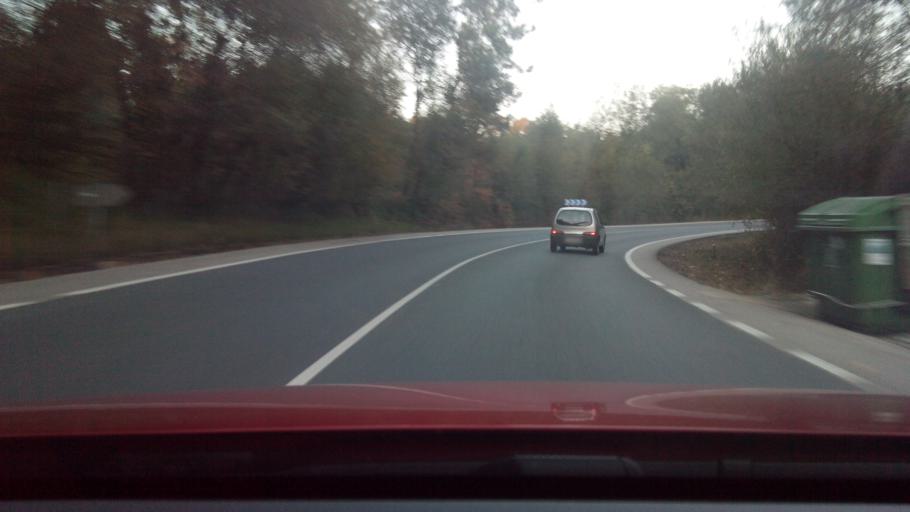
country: ES
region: Galicia
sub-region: Provincia de Pontevedra
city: Gondomar
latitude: 42.1600
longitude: -8.7021
